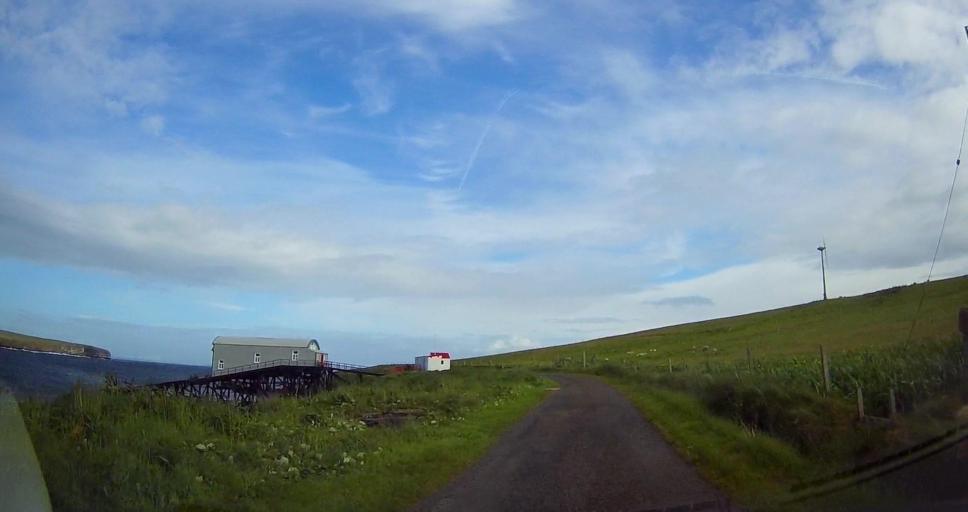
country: GB
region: Scotland
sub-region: Orkney Islands
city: Stromness
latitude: 58.7801
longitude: -3.2299
